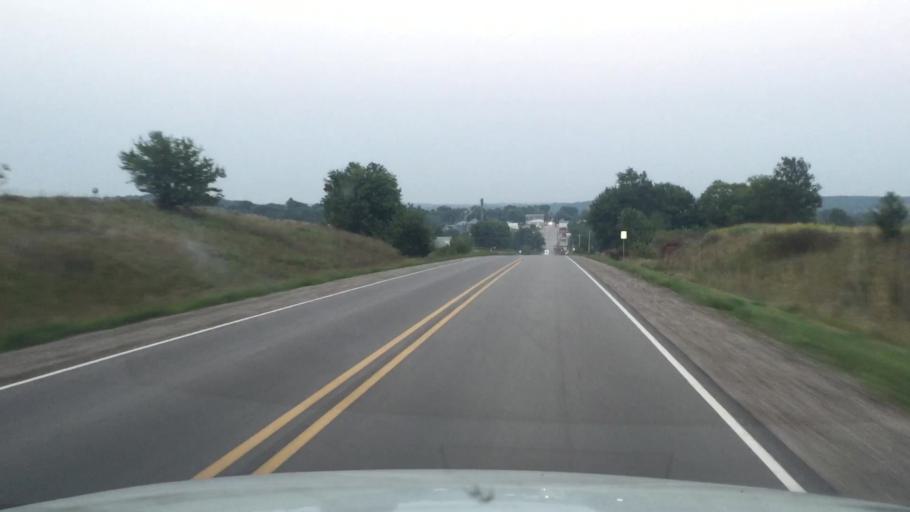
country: US
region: Iowa
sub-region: Marion County
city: Melcher-Dallas
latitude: 41.1895
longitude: -93.3979
